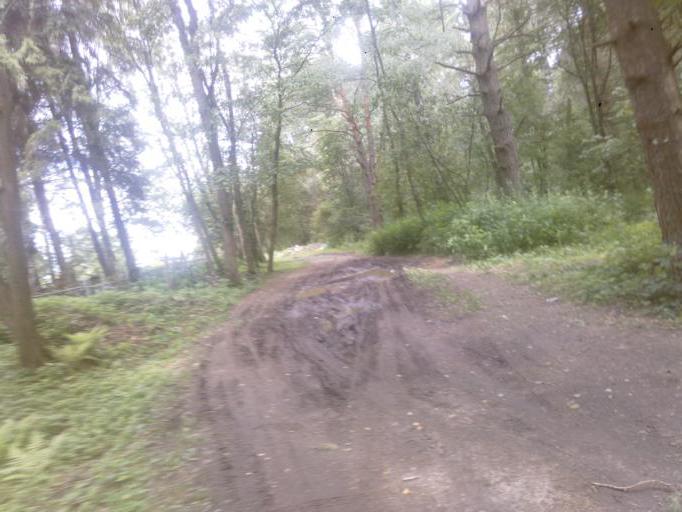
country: RU
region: Moskovskaya
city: Solnechnogorsk
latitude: 56.1383
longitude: 36.9293
